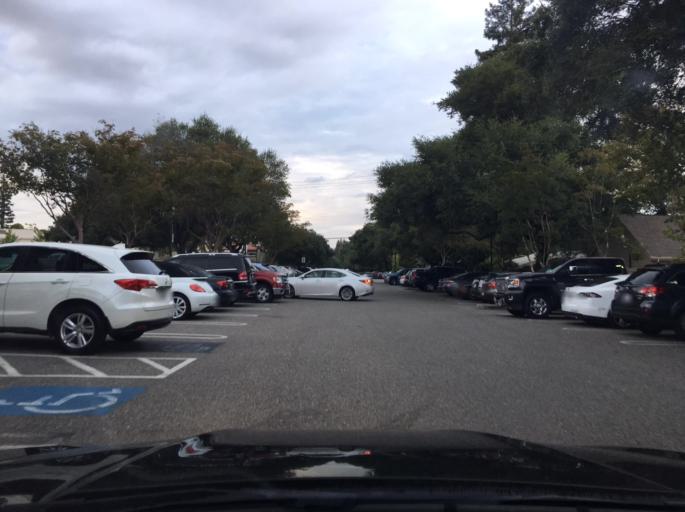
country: US
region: California
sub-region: Santa Clara County
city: Los Gatos
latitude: 37.2250
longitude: -121.9818
